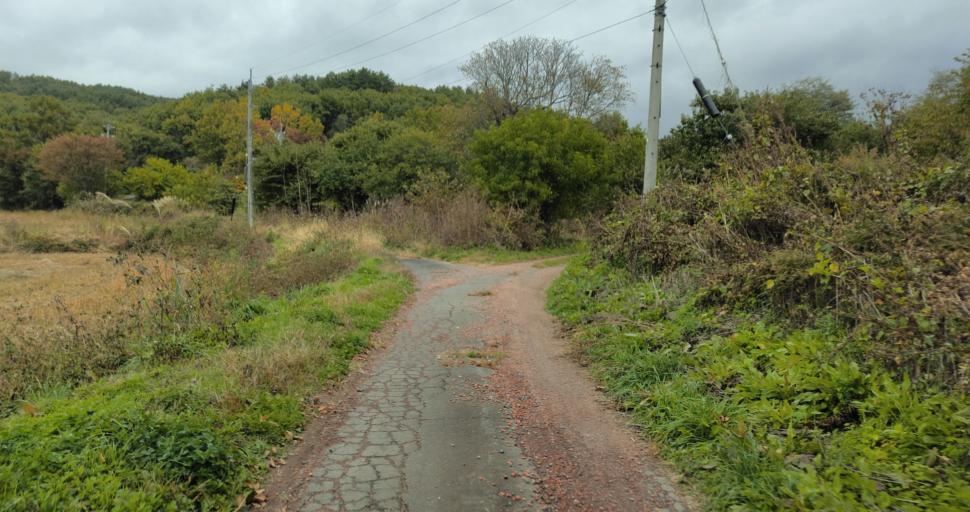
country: JP
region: Nagano
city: Komoro
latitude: 36.3620
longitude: 138.3838
